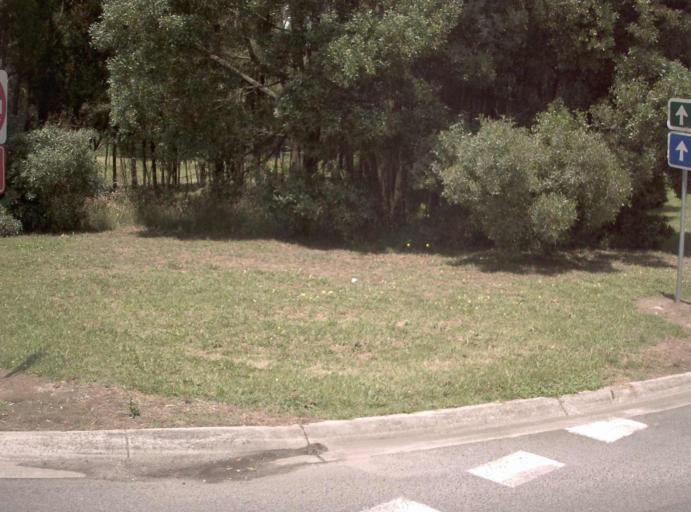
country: AU
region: Victoria
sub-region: Baw Baw
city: Warragul
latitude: -38.1739
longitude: 145.9695
